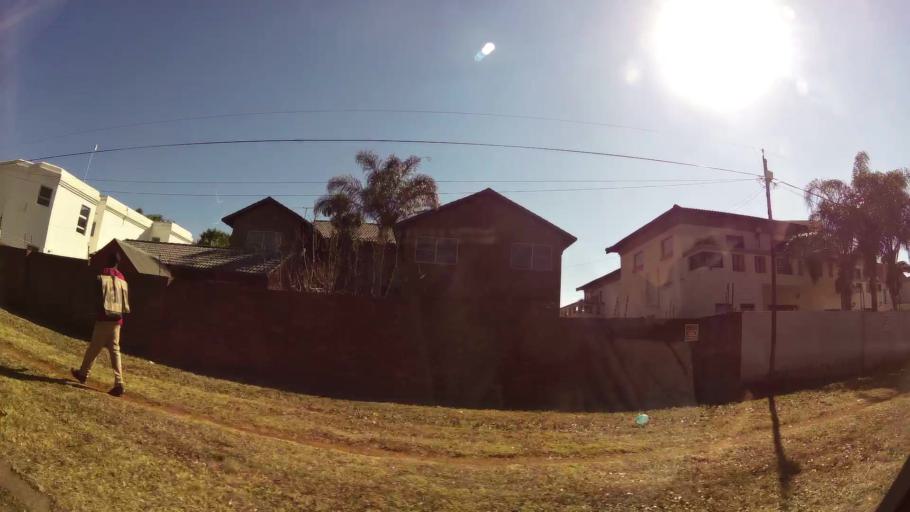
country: ZA
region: Gauteng
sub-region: Ekurhuleni Metropolitan Municipality
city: Germiston
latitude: -26.2976
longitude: 28.1003
